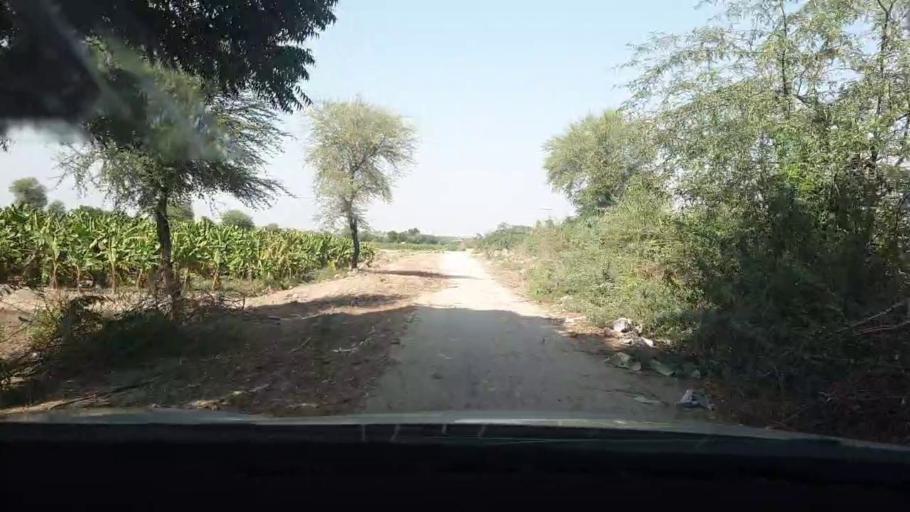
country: PK
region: Sindh
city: Tando Mittha Khan
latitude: 25.8689
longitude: 69.3871
